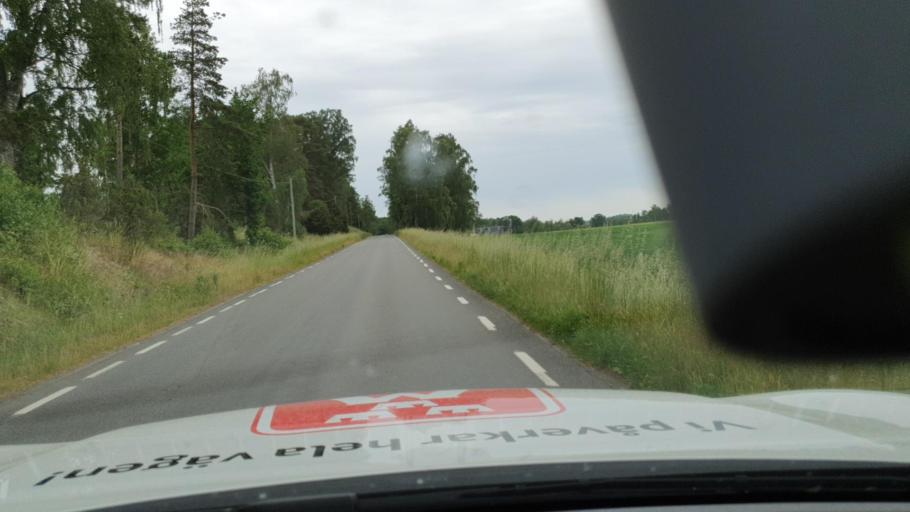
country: SE
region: Vaestra Goetaland
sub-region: Tidaholms Kommun
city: Olofstorp
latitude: 58.3172
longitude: 14.0966
